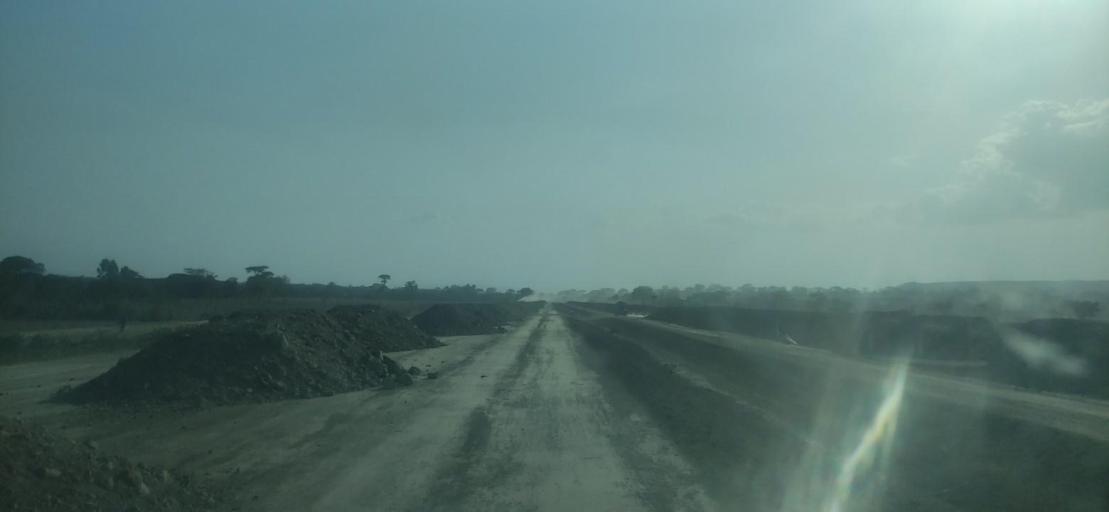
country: ET
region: Southern Nations, Nationalities, and People's Region
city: Hawassa
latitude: 7.1644
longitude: 38.4852
